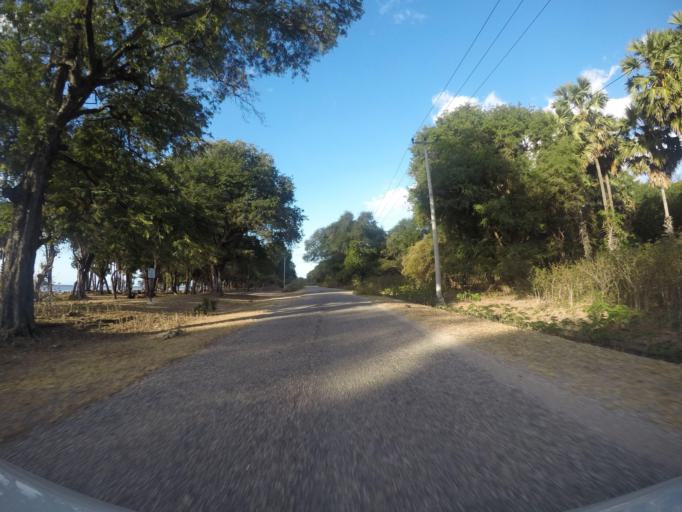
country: TL
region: Lautem
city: Lospalos
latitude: -8.3466
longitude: 126.9248
